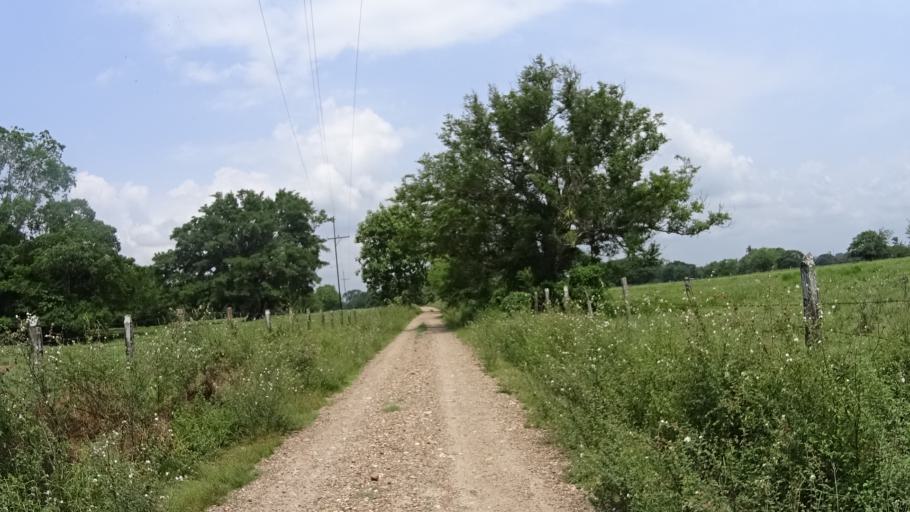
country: CO
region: Cundinamarca
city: Puerto Salgar
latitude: 5.5422
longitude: -74.6682
